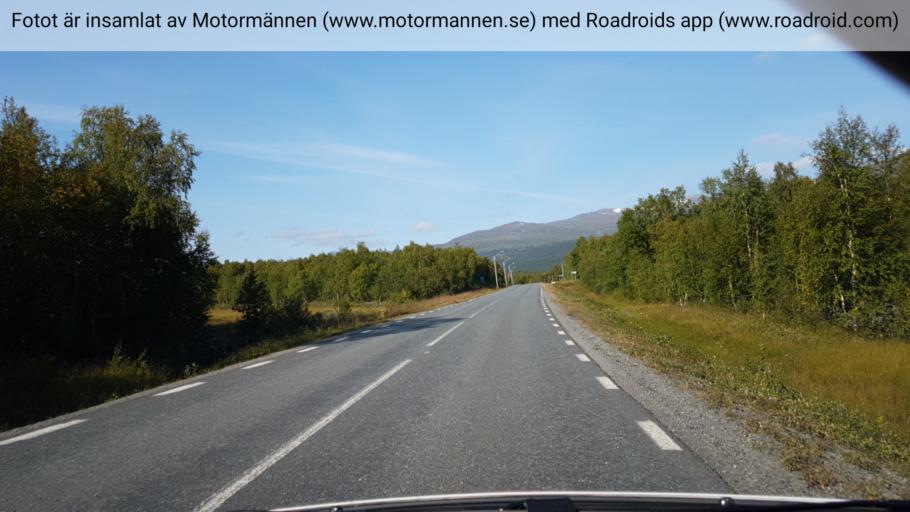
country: NO
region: Nordland
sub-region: Rana
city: Mo i Rana
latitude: 65.7707
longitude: 15.1127
